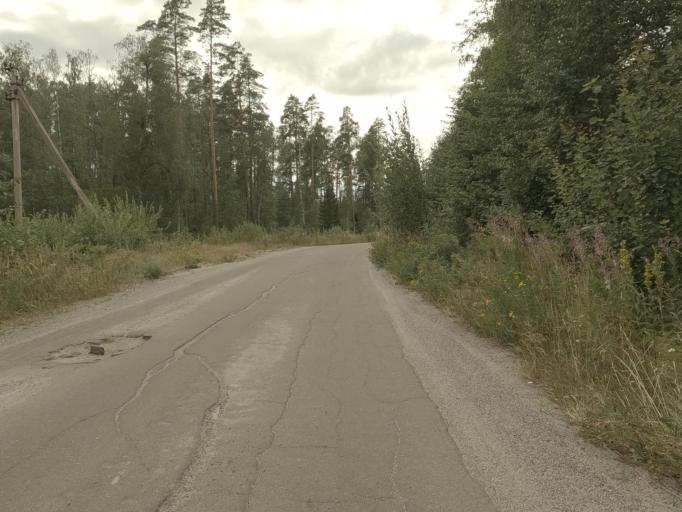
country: RU
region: Leningrad
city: Kamennogorsk
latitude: 60.9712
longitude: 29.1640
